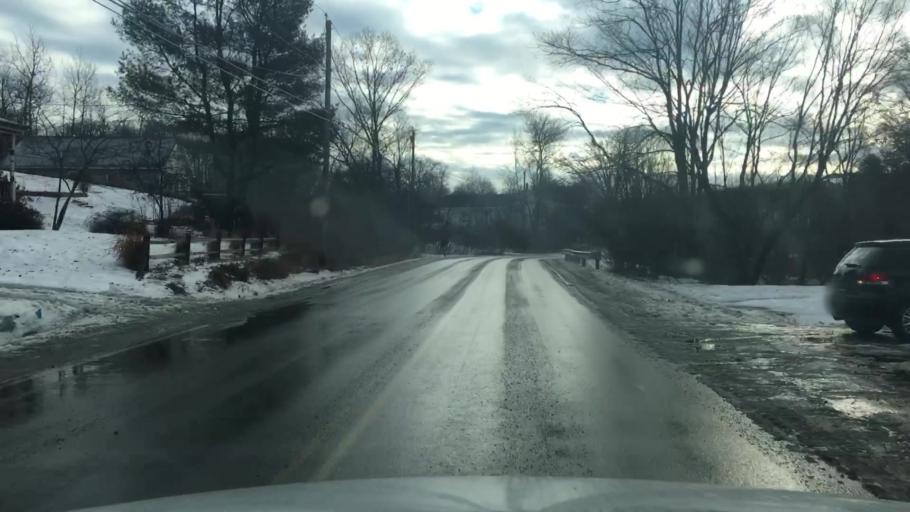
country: US
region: Maine
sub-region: Penobscot County
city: Brewer
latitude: 44.7640
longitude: -68.7766
